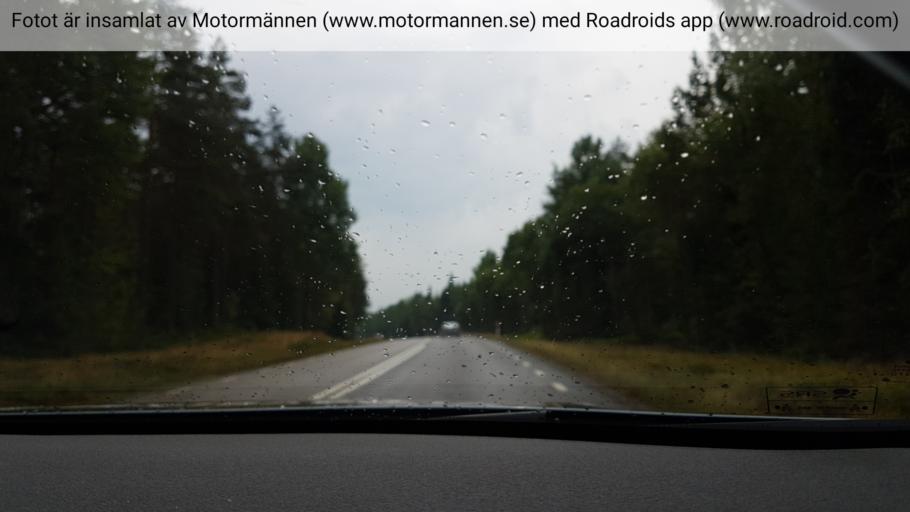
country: SE
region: Joenkoeping
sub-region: Vaggeryds Kommun
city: Vaggeryd
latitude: 57.5292
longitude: 14.2745
